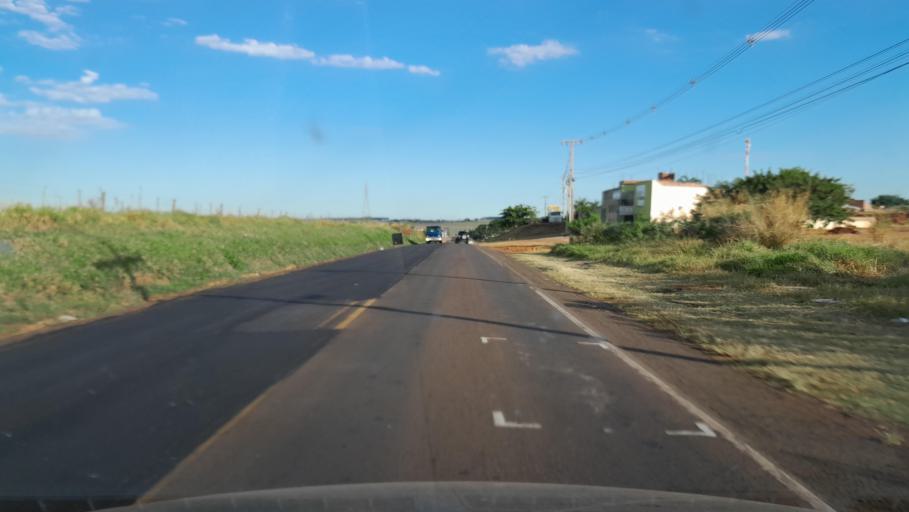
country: BR
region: Parana
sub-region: Umuarama
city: Umuarama
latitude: -23.7673
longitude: -53.2697
